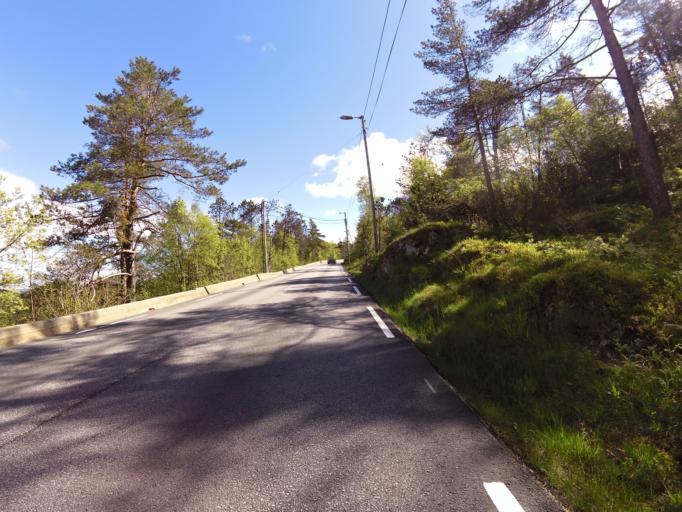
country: NO
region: Hordaland
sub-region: Bergen
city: Sandsli
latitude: 60.2568
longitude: 5.3575
